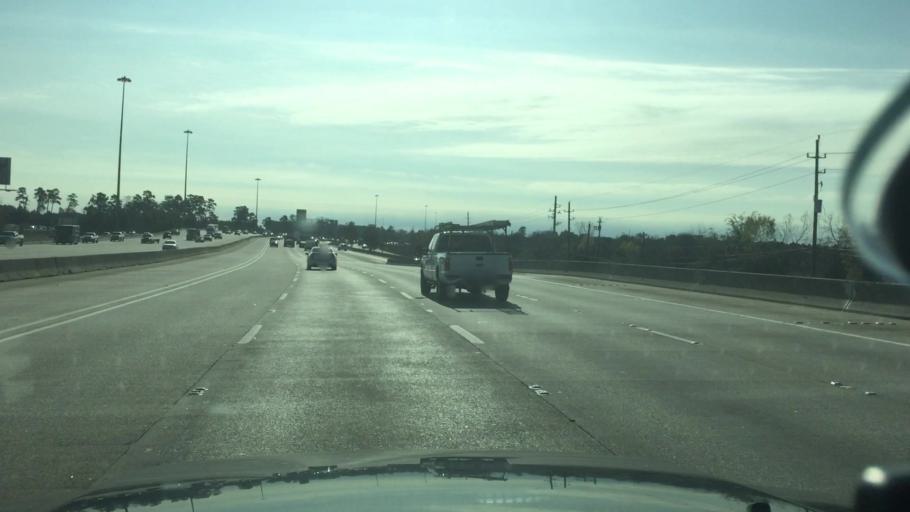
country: US
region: Texas
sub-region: Montgomery County
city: Oak Ridge North
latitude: 30.1174
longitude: -95.4406
